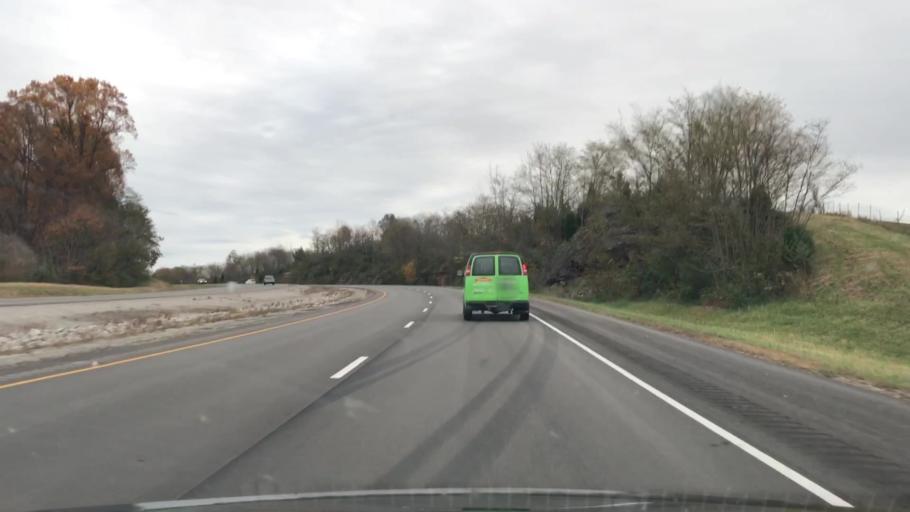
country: US
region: Kentucky
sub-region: Barren County
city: Glasgow
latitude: 37.0278
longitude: -85.9269
